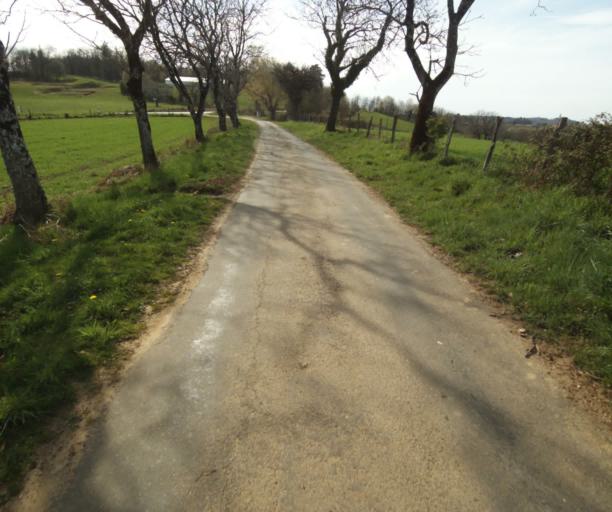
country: FR
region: Limousin
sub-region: Departement de la Correze
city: Naves
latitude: 45.3341
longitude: 1.7610
